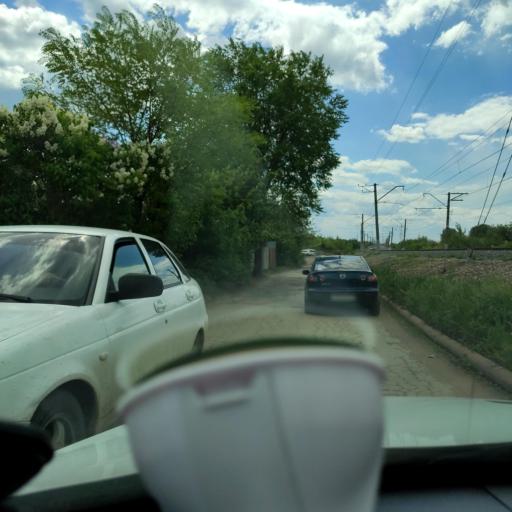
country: RU
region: Samara
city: Petra-Dubrava
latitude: 53.2671
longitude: 50.3157
